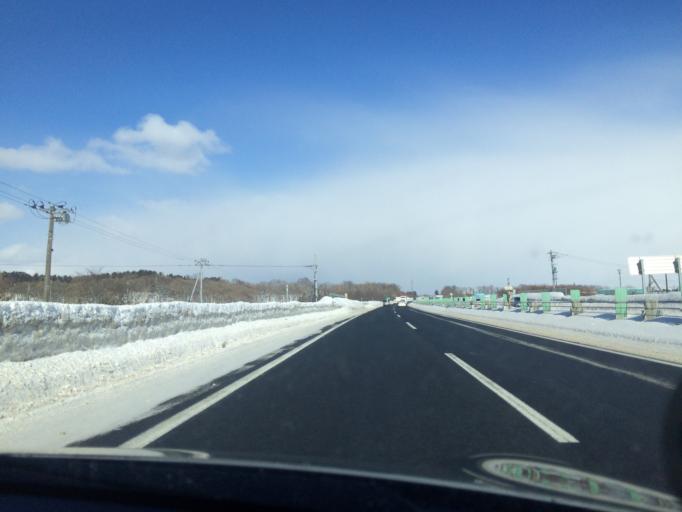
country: JP
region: Hokkaido
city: Kitahiroshima
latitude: 42.8892
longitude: 141.5492
